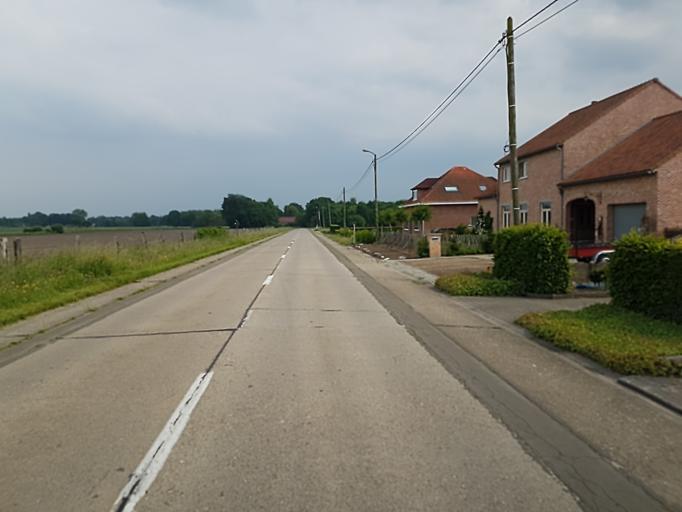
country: BE
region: Flanders
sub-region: Provincie Antwerpen
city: Putte
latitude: 51.0805
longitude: 4.6485
